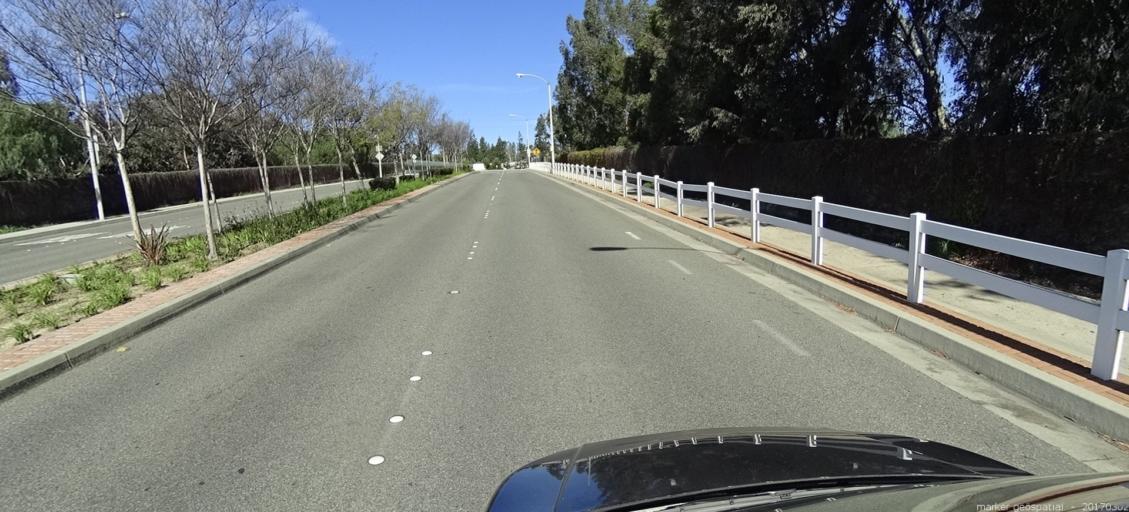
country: US
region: California
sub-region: Orange County
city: Yorba Linda
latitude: 33.8649
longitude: -117.7763
